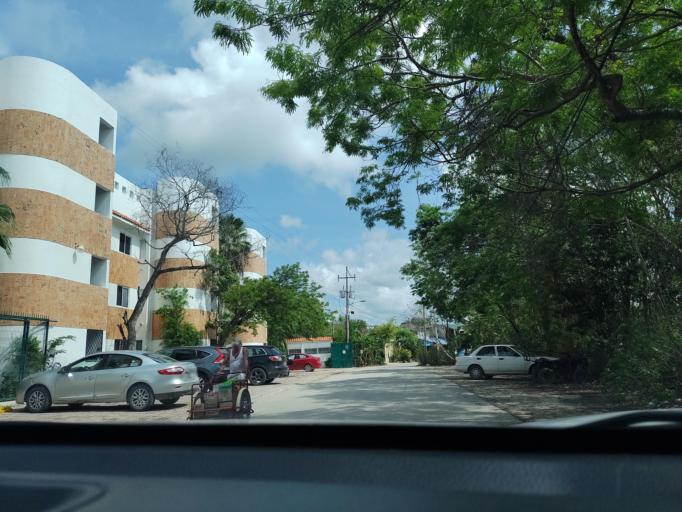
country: MX
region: Quintana Roo
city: Tulum
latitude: 20.2101
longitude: -87.4734
